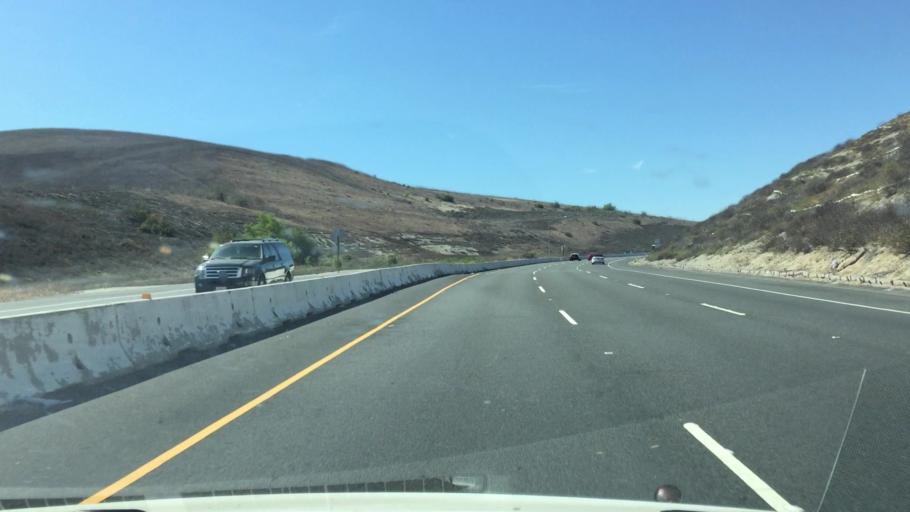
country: US
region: California
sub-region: Orange County
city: North Tustin
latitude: 33.7533
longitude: -117.7315
